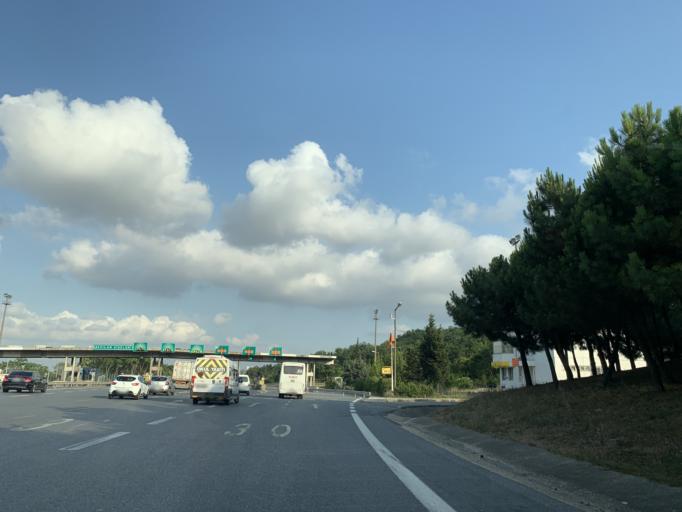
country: TR
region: Istanbul
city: Esenyurt
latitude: 41.0506
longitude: 28.6862
